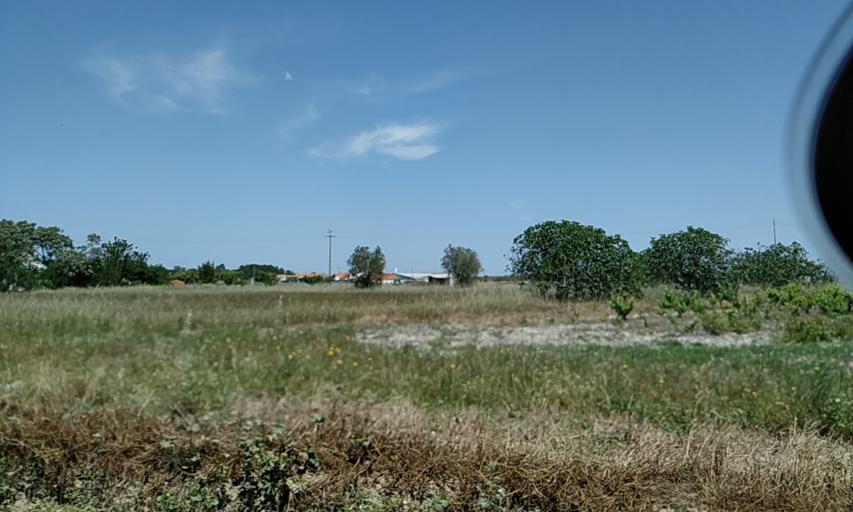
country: PT
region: Setubal
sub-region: Palmela
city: Pinhal Novo
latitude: 38.6449
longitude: -8.7438
